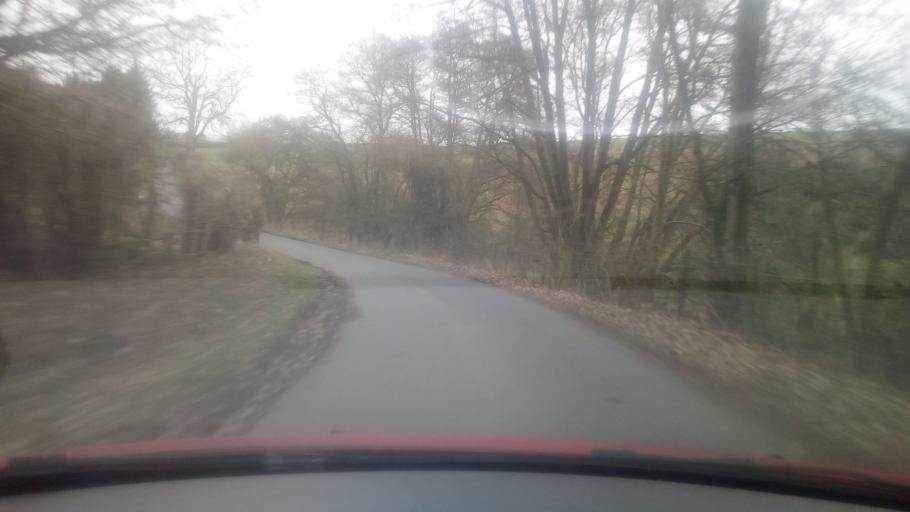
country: GB
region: Scotland
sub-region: The Scottish Borders
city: Hawick
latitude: 55.4382
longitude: -2.6904
